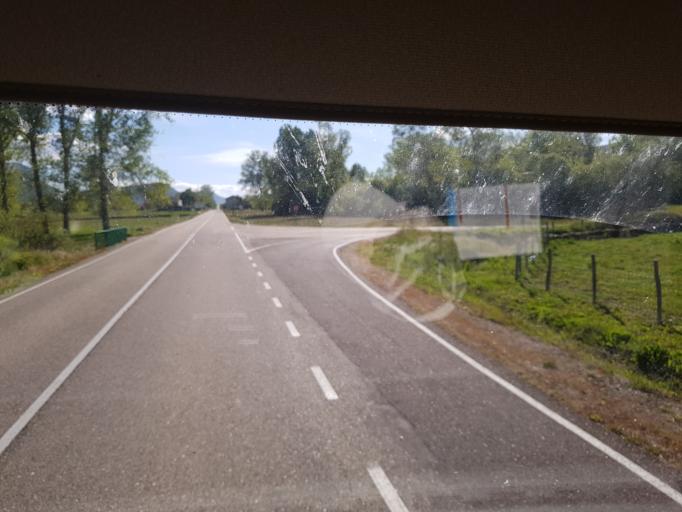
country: ES
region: Castille and Leon
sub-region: Provincia de Burgos
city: Espinosa de los Monteros
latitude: 43.0641
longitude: -3.5799
